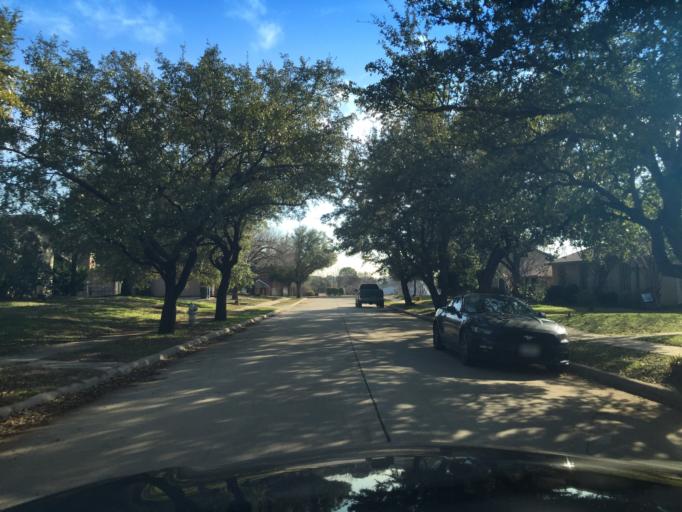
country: US
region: Texas
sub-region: Dallas County
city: Carrollton
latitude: 32.9931
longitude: -96.8922
